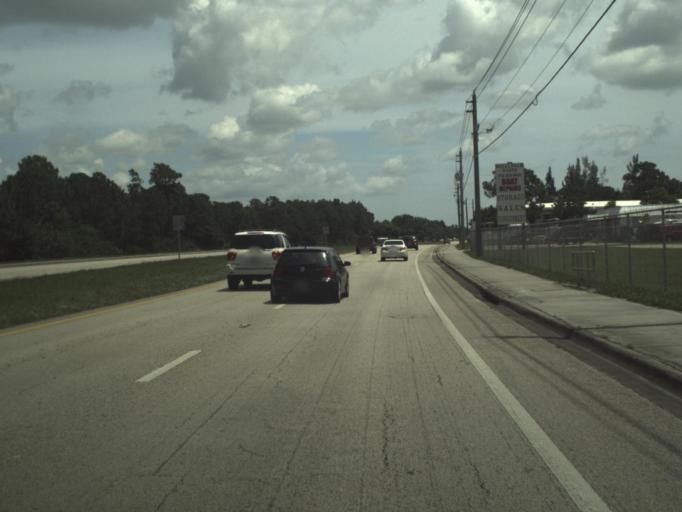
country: US
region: Florida
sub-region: Martin County
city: Palm City
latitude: 27.1329
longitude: -80.2508
